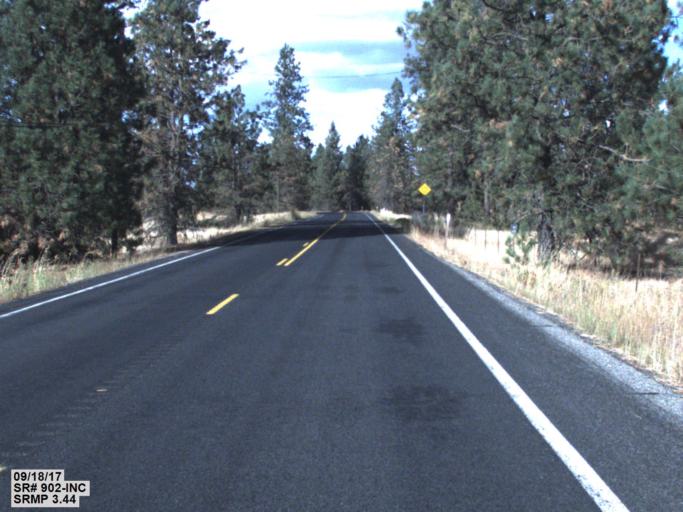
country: US
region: Washington
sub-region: Spokane County
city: Medical Lake
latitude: 47.5417
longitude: -117.7063
